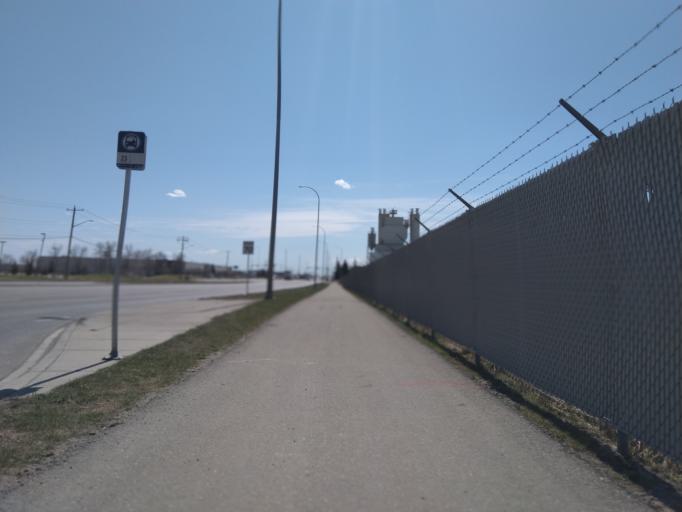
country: CA
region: Alberta
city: Calgary
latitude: 50.9747
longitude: -113.9588
